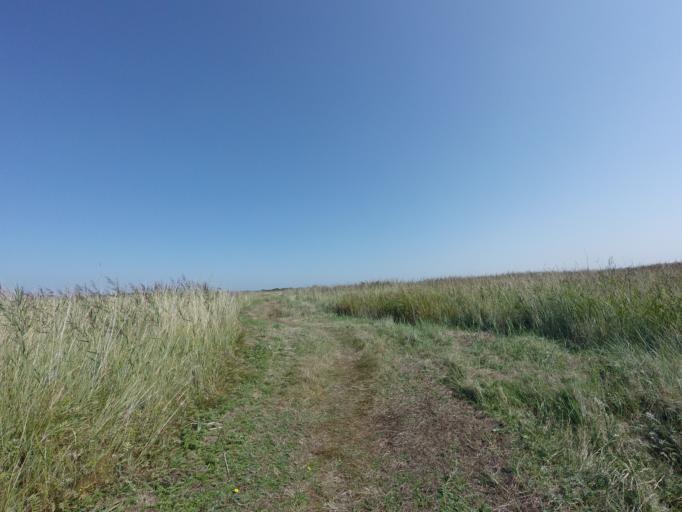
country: NL
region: Friesland
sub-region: Gemeente Schiermonnikoog
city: Schiermonnikoog
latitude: 53.4923
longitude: 6.2426
